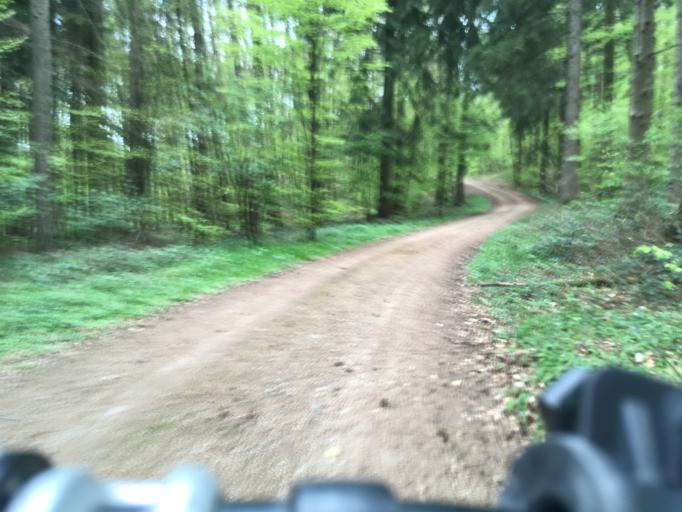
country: CH
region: Thurgau
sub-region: Frauenfeld District
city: Diessenhofen
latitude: 47.7090
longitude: 8.7316
